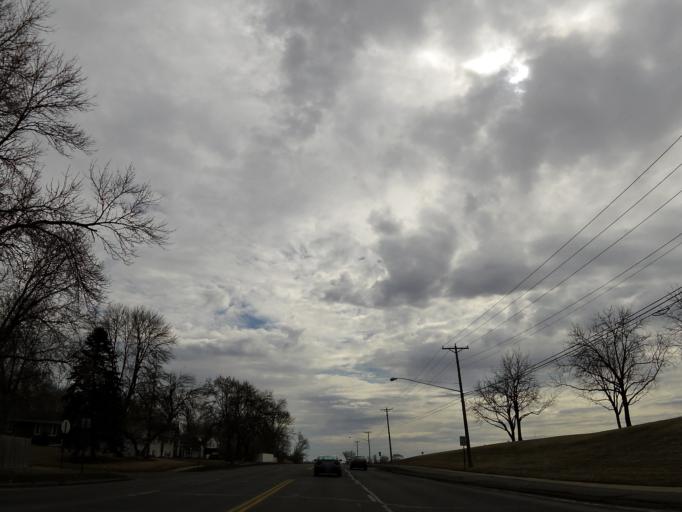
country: US
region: Minnesota
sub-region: Hennepin County
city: Bloomington
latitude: 44.8187
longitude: -93.3296
